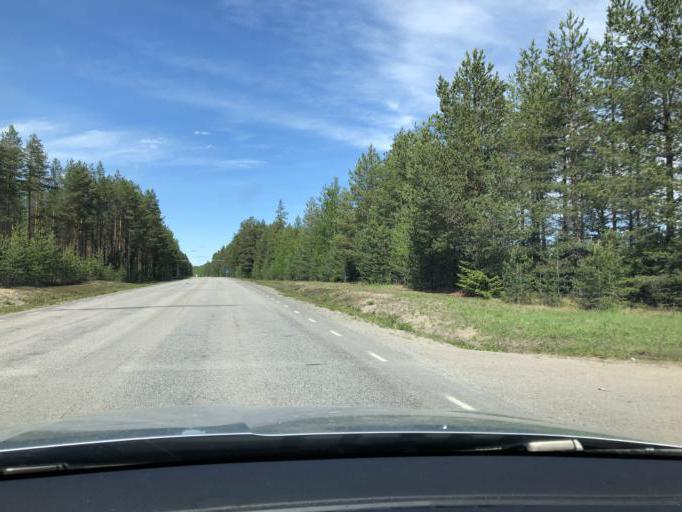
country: SE
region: Norrbotten
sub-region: Pitea Kommun
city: Bergsviken
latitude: 65.3749
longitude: 21.3499
